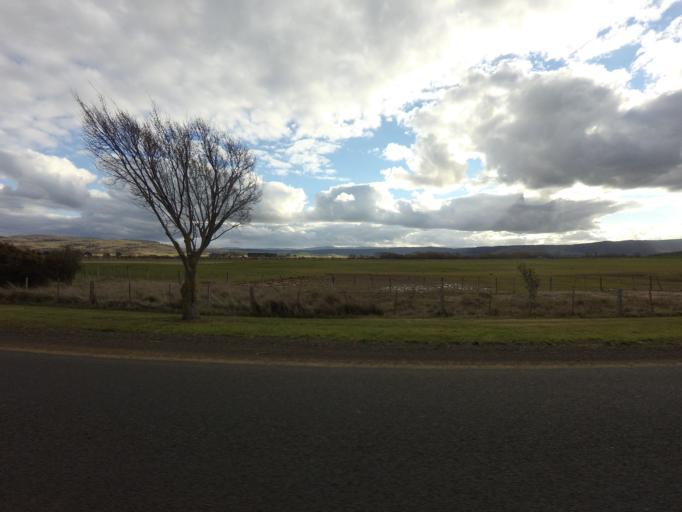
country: AU
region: Tasmania
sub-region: Northern Midlands
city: Evandale
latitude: -42.0227
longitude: 147.4928
